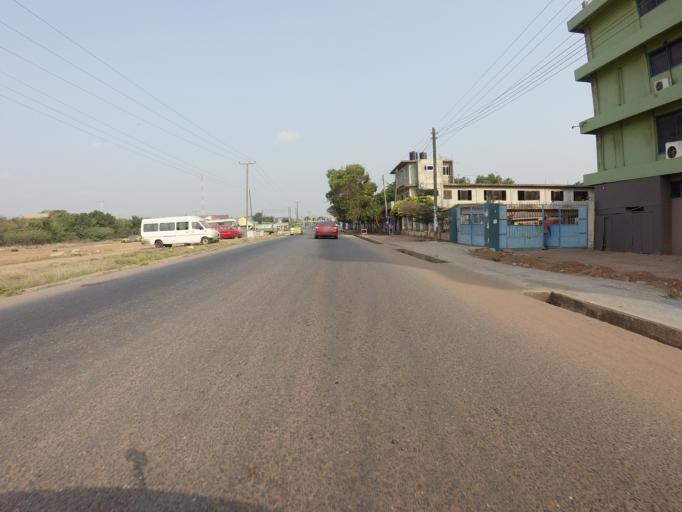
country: GH
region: Greater Accra
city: Teshi Old Town
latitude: 5.5729
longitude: -0.1445
